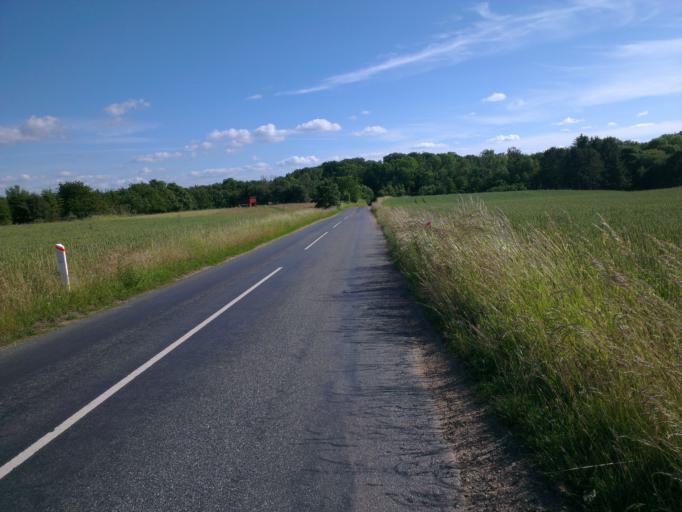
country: DK
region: Capital Region
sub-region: Frederikssund Kommune
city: Jaegerspris
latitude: 55.8259
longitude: 11.9617
